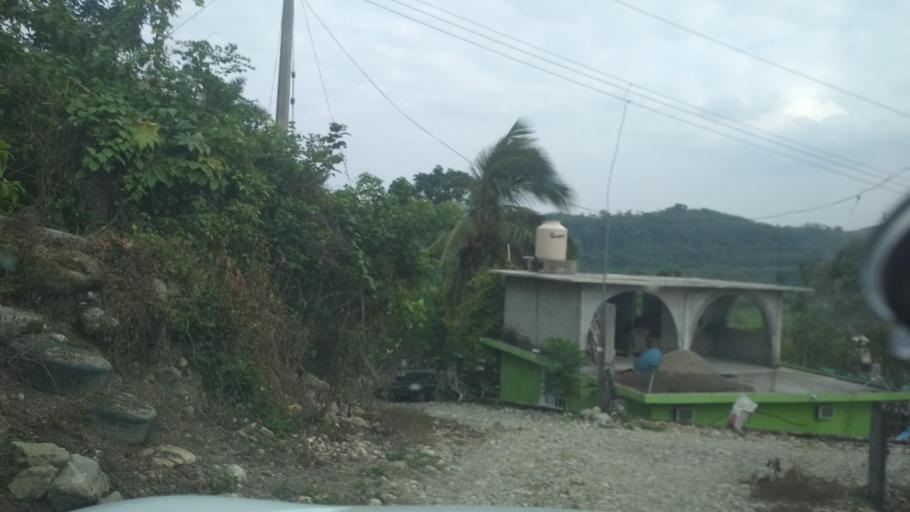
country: MX
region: Veracruz
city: Papantla de Olarte
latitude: 20.5131
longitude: -97.3373
